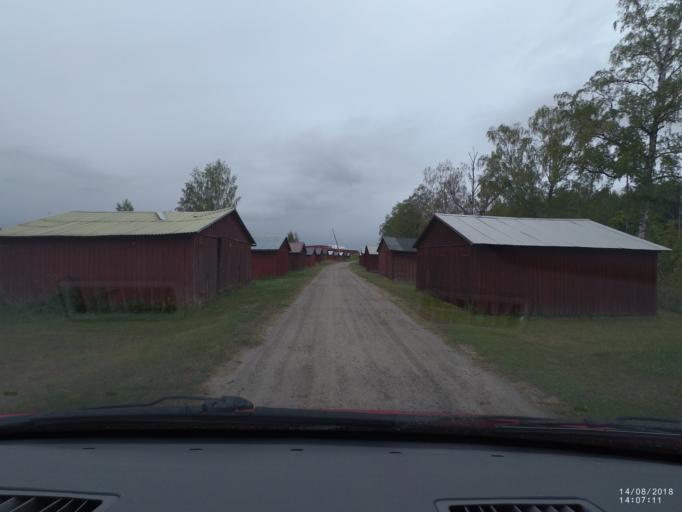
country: SE
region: Soedermanland
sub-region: Nykopings Kommun
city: Nykoping
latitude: 58.7566
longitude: 16.9775
